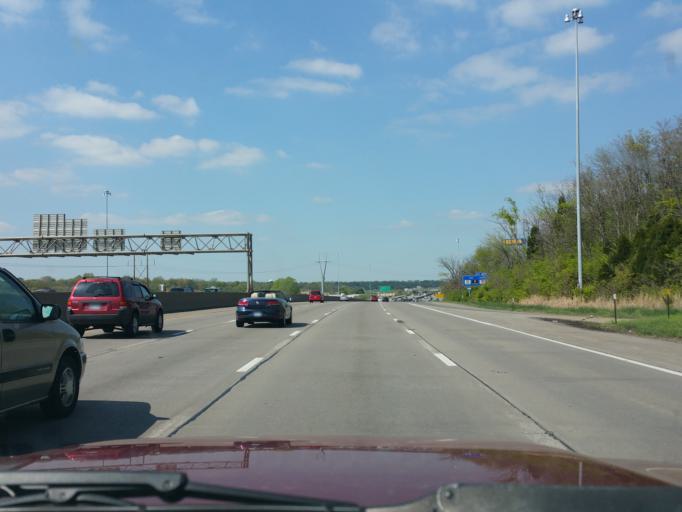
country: US
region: Kansas
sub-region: Johnson County
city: Merriam
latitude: 39.0164
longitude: -94.6929
